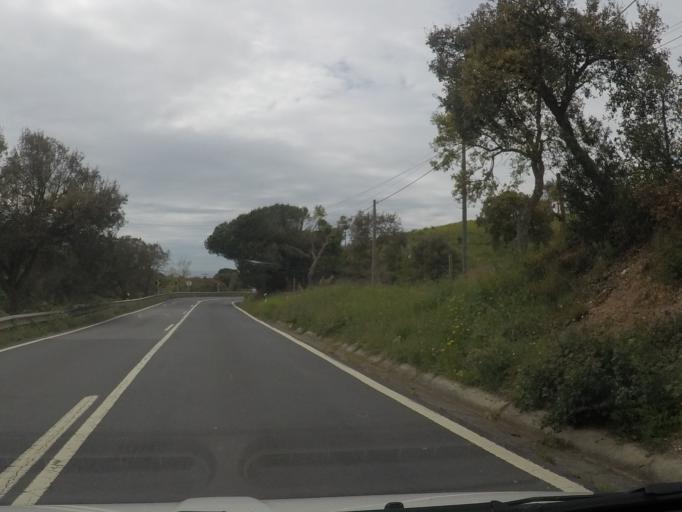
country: PT
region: Setubal
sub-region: Sines
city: Porto Covo
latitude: 37.8674
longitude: -8.7351
